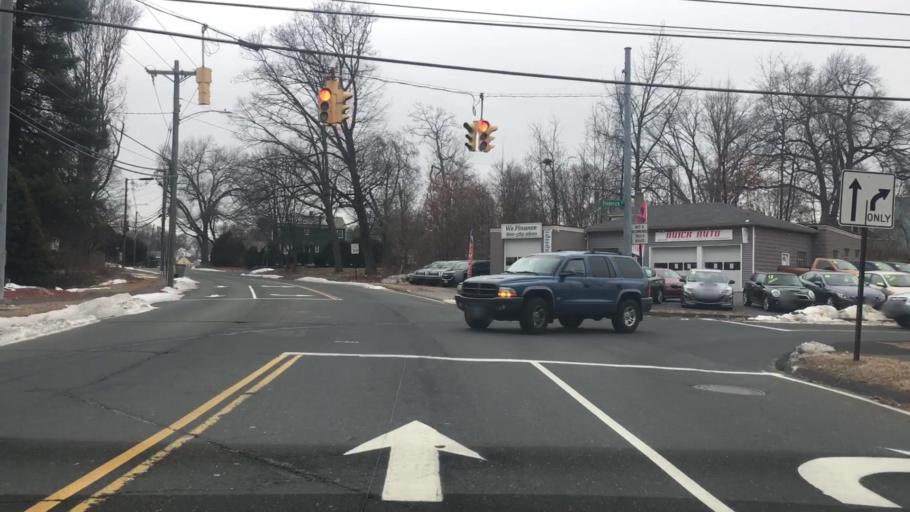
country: US
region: Connecticut
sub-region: Hartford County
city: Bristol
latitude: 41.6740
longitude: -72.9128
